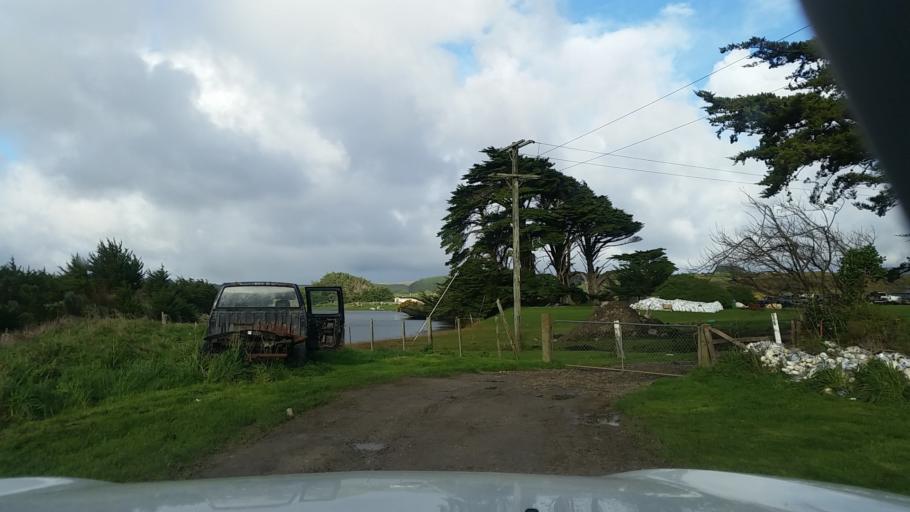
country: NZ
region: Chatham Islands
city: Waitangi
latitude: -43.9564
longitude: -176.5558
